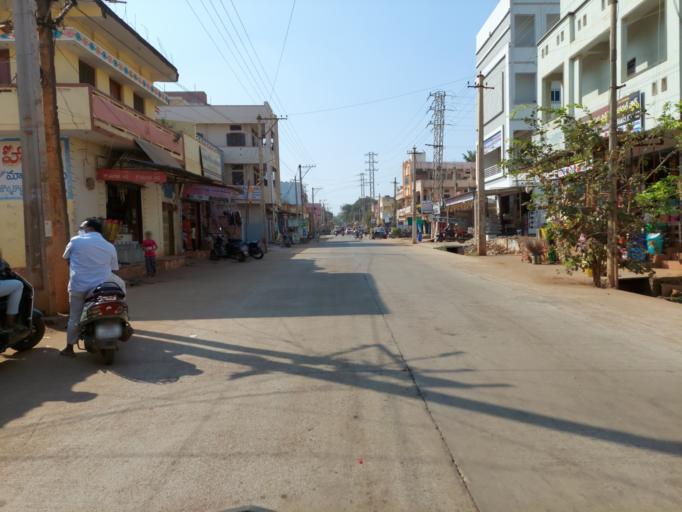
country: IN
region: Telangana
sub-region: Rangareddi
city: Vikarabad
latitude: 17.3372
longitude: 77.9029
